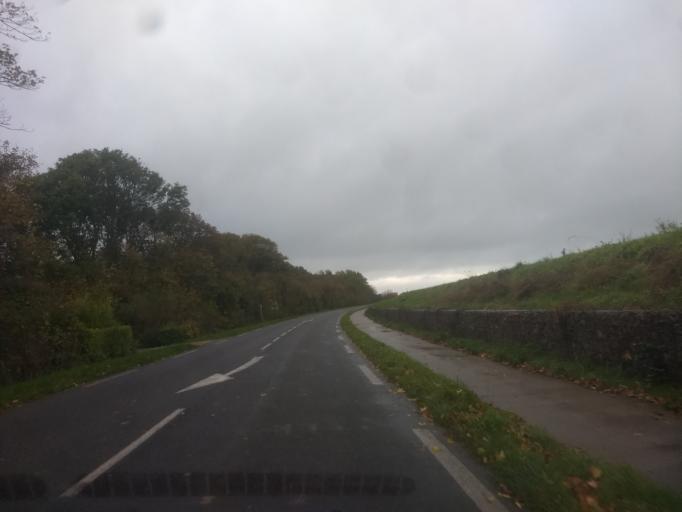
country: FR
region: Nord-Pas-de-Calais
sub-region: Departement du Pas-de-Calais
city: Wissant
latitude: 50.8964
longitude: 1.6858
